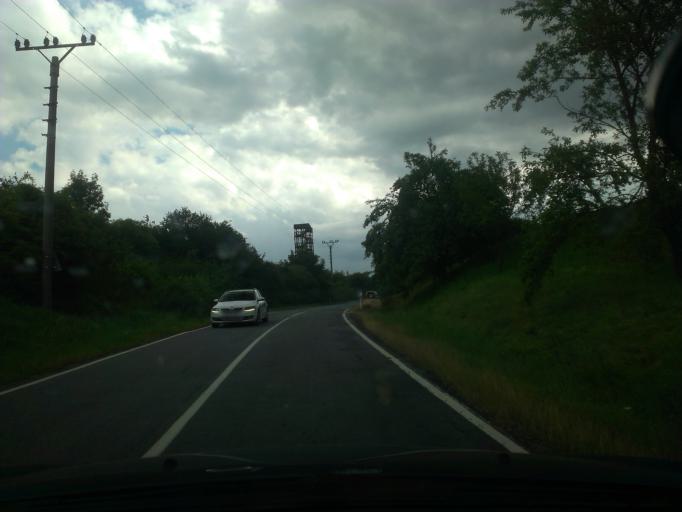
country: CZ
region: South Moravian
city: Velka nad Velickou
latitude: 48.8608
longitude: 17.5228
